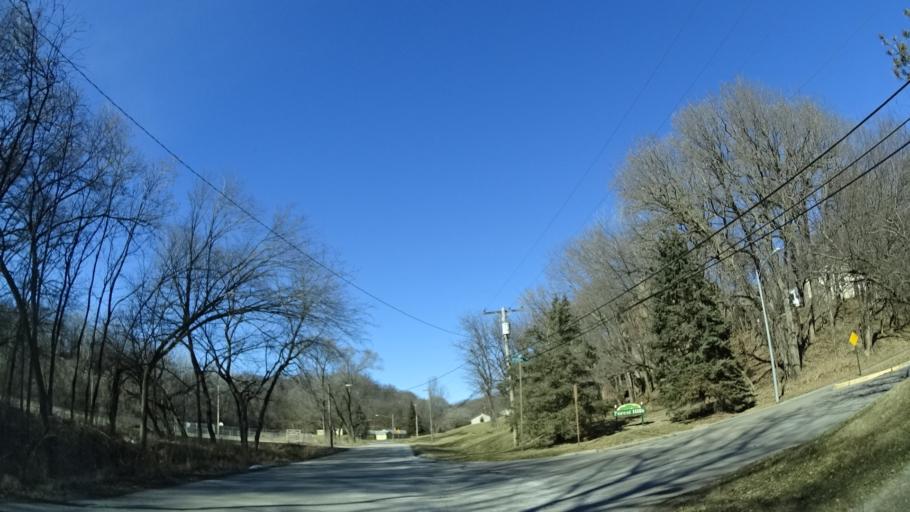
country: US
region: Nebraska
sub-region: Sarpy County
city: Bellevue
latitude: 41.1535
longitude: -95.8941
